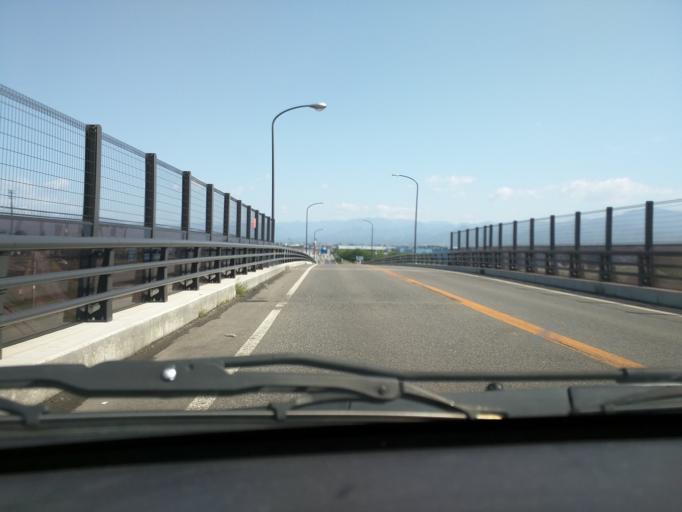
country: JP
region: Fukushima
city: Kitakata
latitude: 37.5825
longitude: 139.8929
